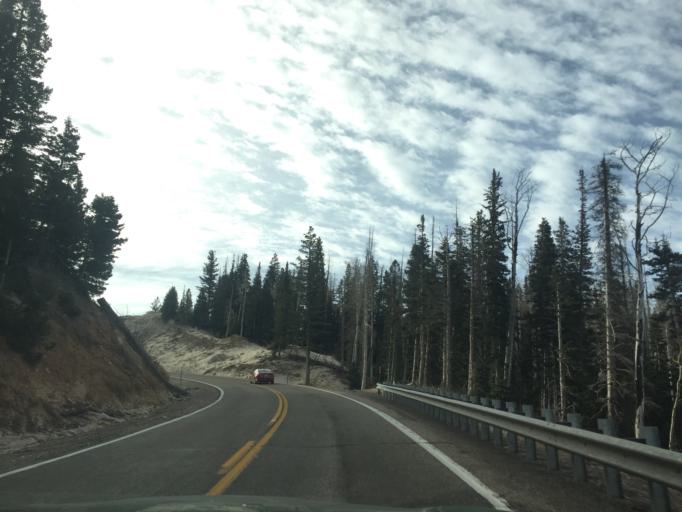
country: US
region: Utah
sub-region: Iron County
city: Cedar City
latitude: 37.5840
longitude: -112.8839
